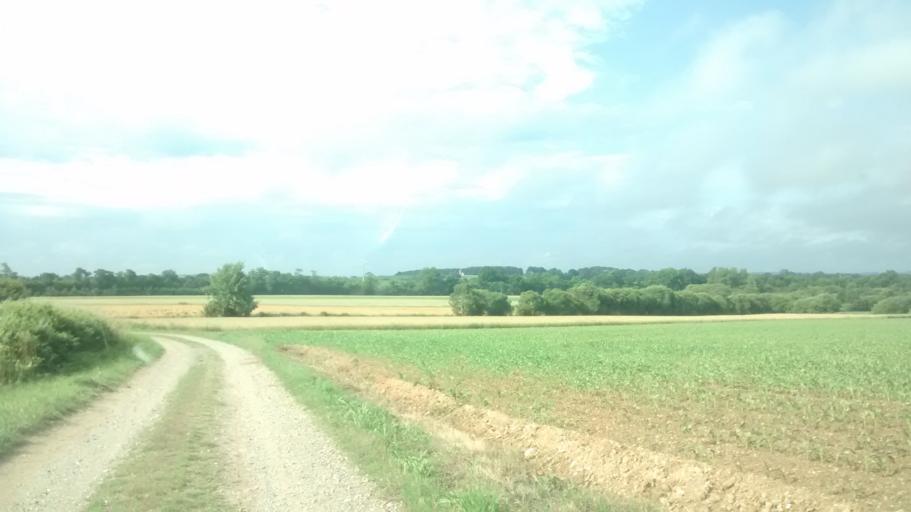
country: FR
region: Brittany
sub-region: Departement d'Ille-et-Vilaine
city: Plechatel
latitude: 47.8387
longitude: -1.7465
